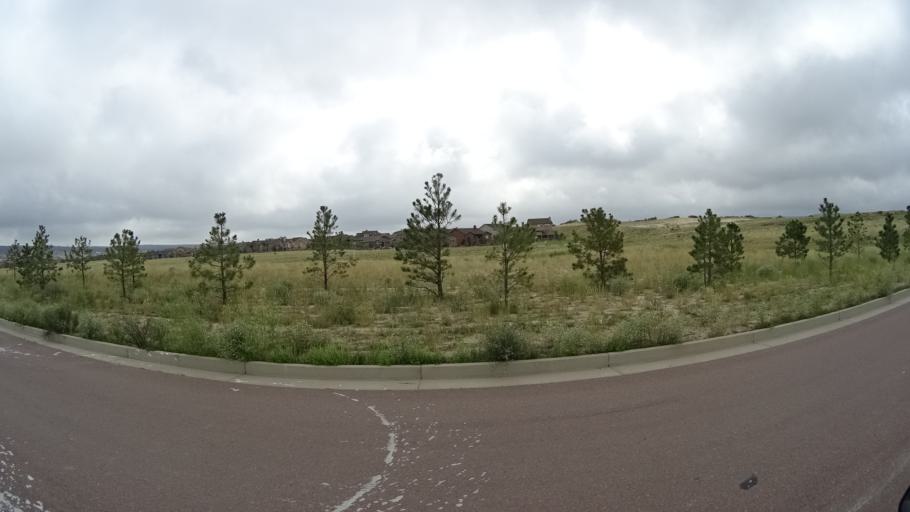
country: US
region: Colorado
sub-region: El Paso County
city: Gleneagle
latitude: 39.0141
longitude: -104.7862
